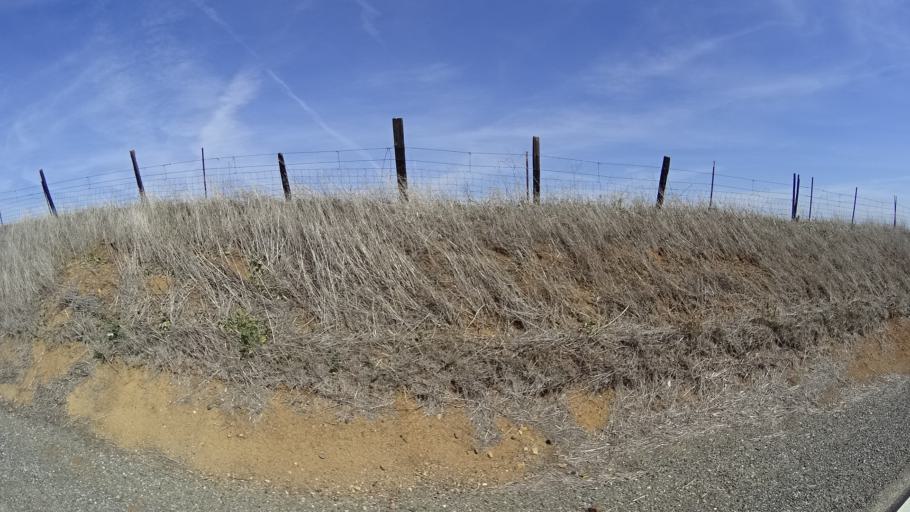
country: US
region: California
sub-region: Glenn County
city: Willows
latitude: 39.5315
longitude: -122.3187
